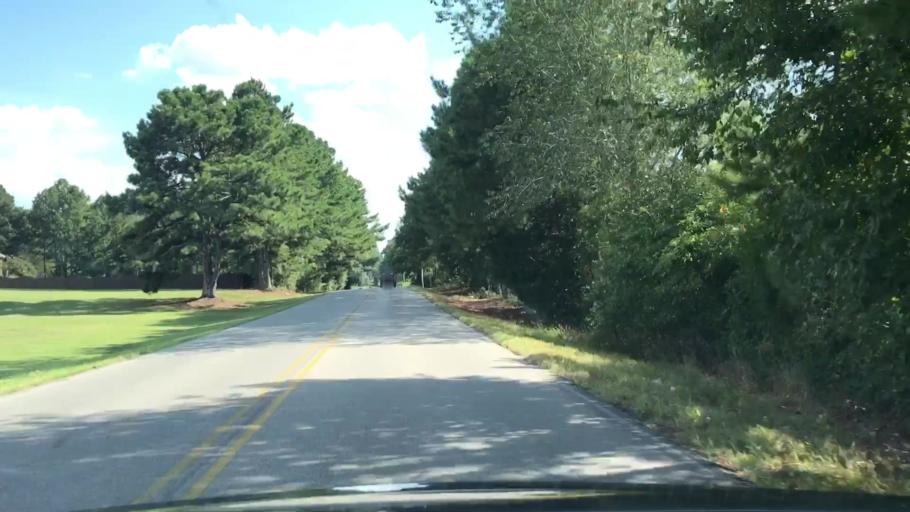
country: US
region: Alabama
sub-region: Madison County
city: Harvest
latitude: 34.8908
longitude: -86.7487
